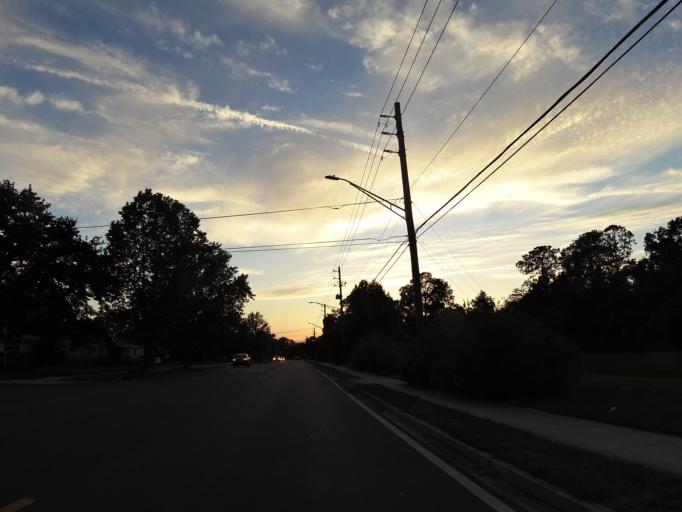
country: US
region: Florida
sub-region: Duval County
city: Jacksonville
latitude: 30.2703
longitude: -81.6011
